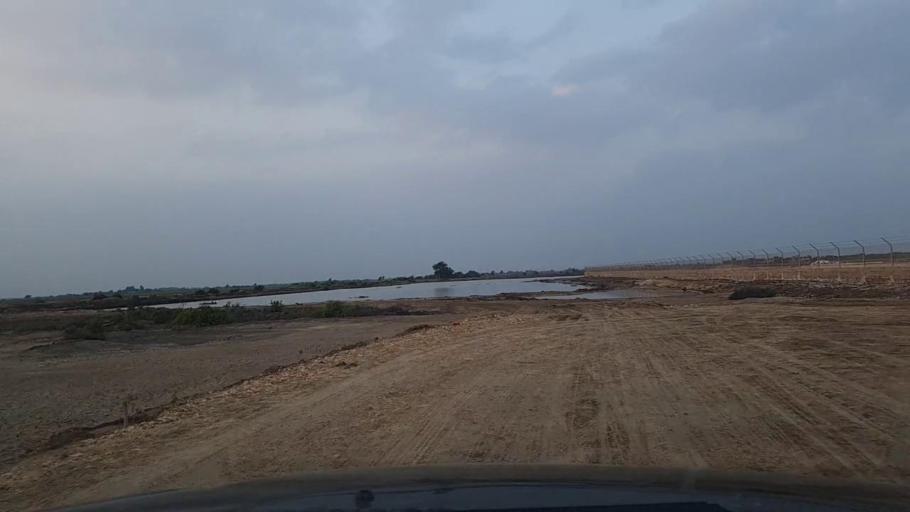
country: PK
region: Sindh
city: Jati
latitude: 24.4942
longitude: 68.3918
